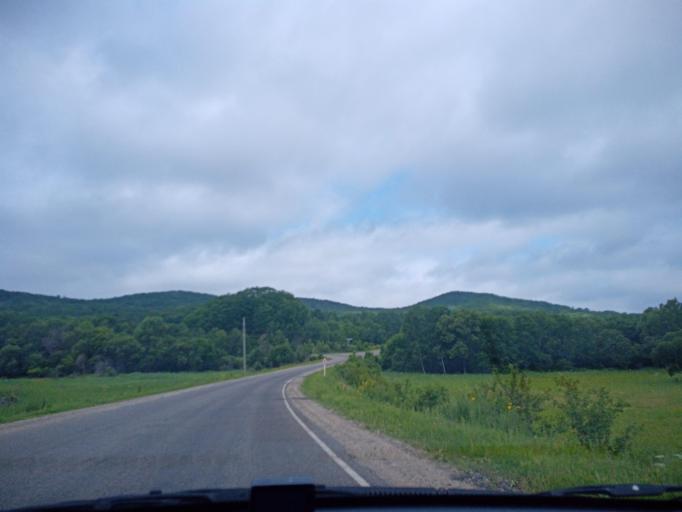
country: RU
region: Primorskiy
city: Novopokrovka
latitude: 45.8423
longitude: 134.4502
